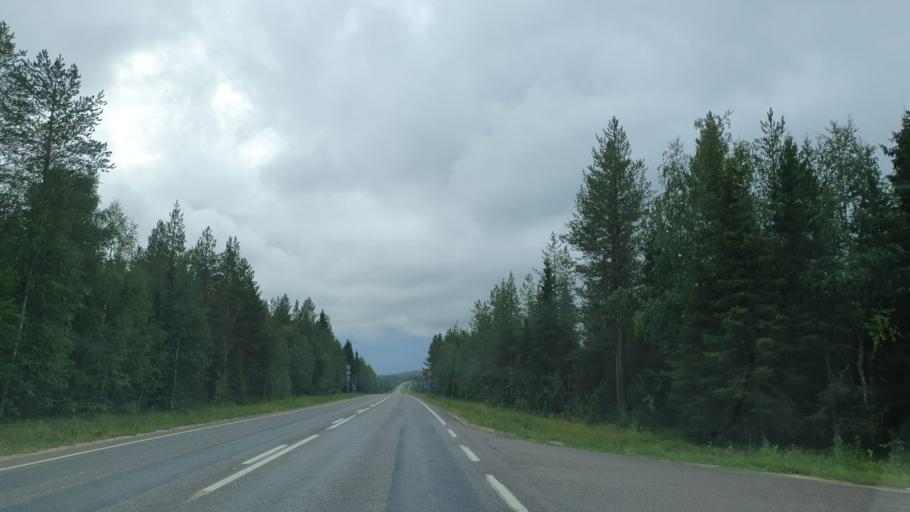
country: FI
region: Lapland
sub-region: Tunturi-Lappi
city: Kolari
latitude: 67.2093
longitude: 23.9065
